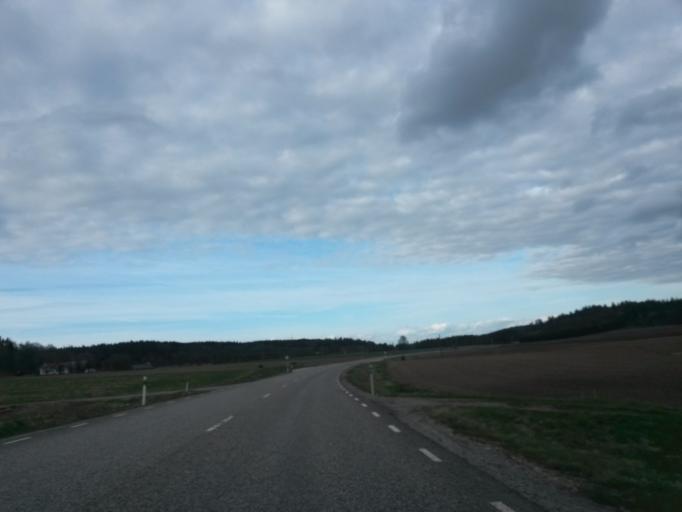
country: SE
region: Vaestra Goetaland
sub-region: Vargarda Kommun
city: Jonstorp
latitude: 58.0553
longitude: 12.6623
